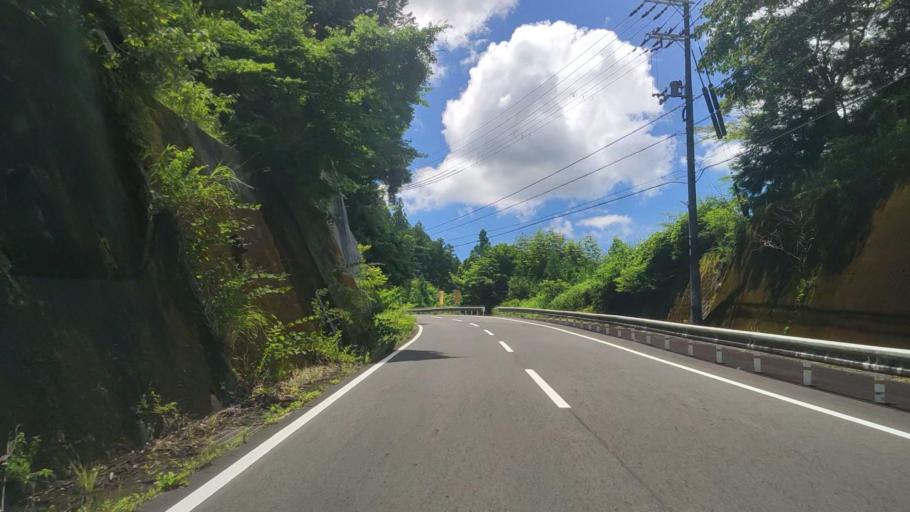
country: JP
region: Mie
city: Owase
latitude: 33.9542
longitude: 136.0688
